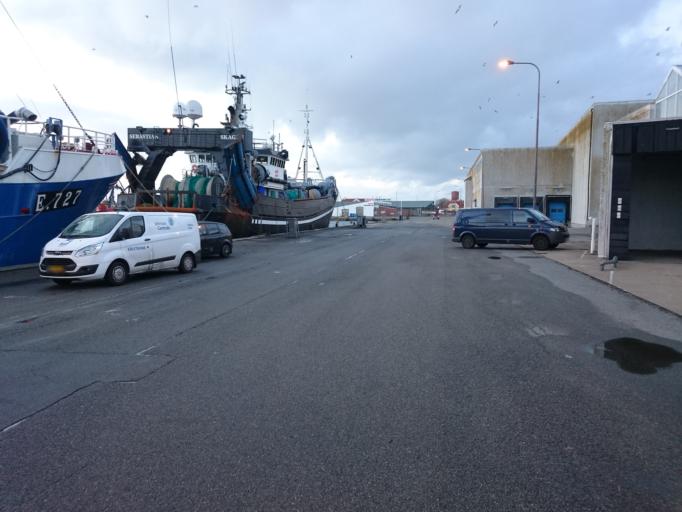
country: DK
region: North Denmark
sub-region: Frederikshavn Kommune
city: Skagen
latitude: 57.7213
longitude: 10.6026
